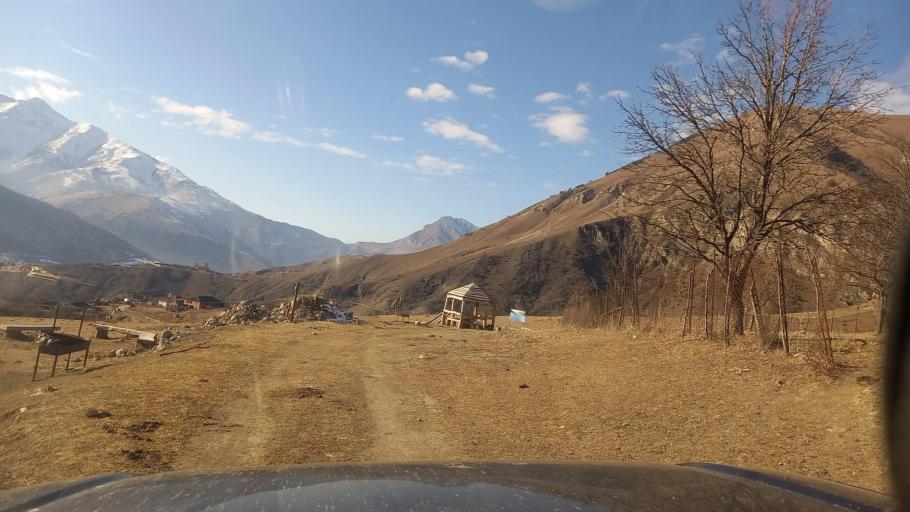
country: RU
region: Ingushetiya
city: Dzhayrakh
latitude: 42.8361
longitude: 44.7206
